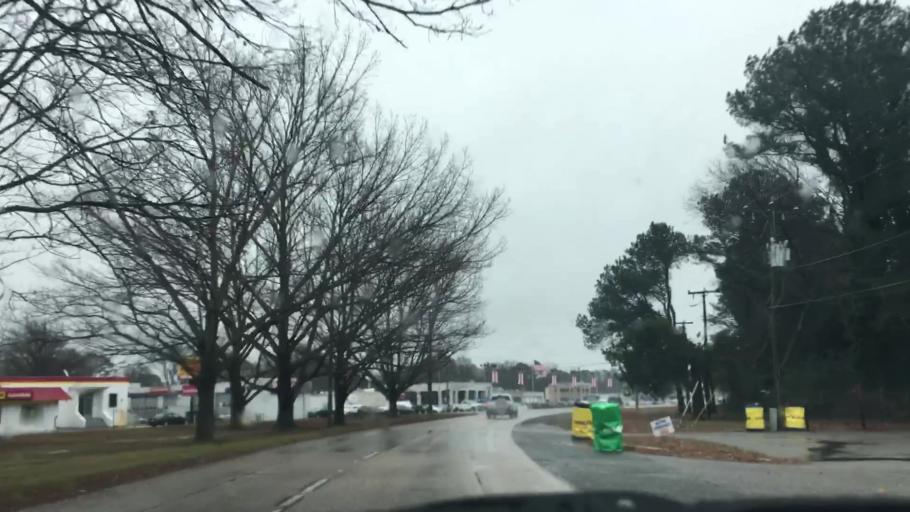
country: US
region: Virginia
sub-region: City of Norfolk
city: Norfolk
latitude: 36.9143
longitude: -76.2384
